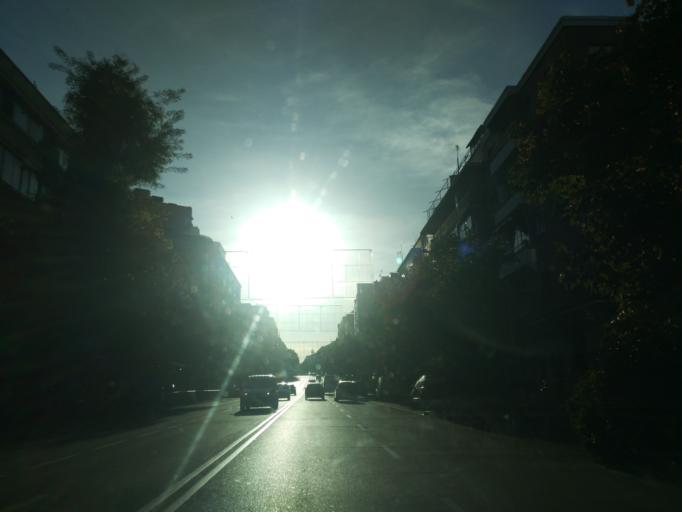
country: ES
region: Madrid
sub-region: Provincia de Madrid
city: Carabanchel
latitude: 40.3933
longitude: -3.7239
